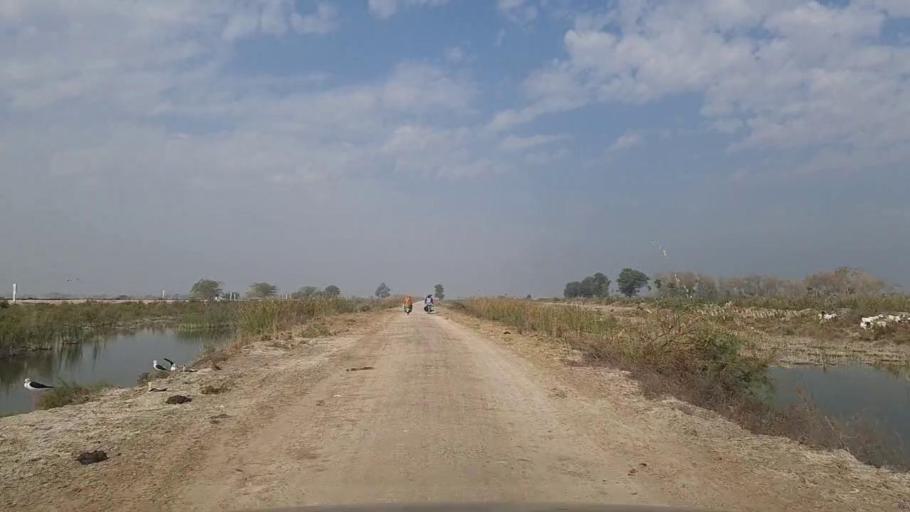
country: PK
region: Sindh
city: Daur
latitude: 26.3953
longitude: 68.3483
